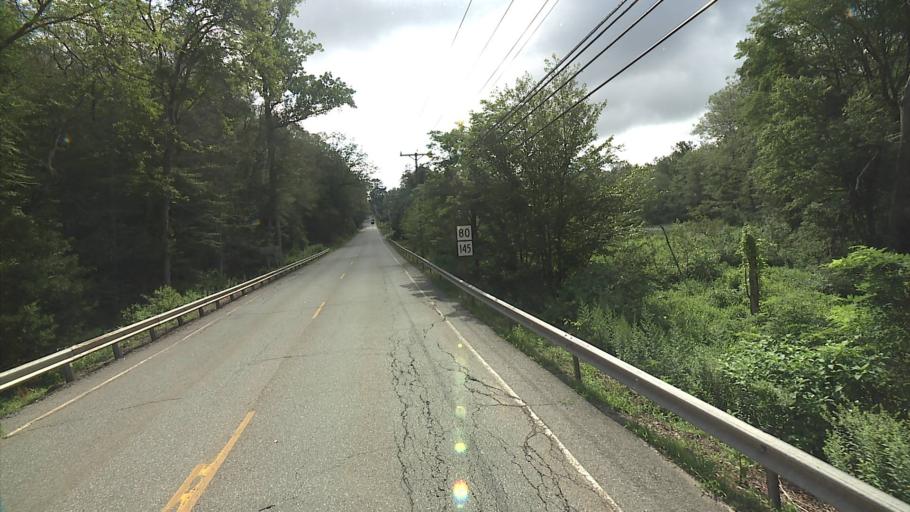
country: US
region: Connecticut
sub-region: Middlesex County
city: Chester Center
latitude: 41.3594
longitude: -72.4992
